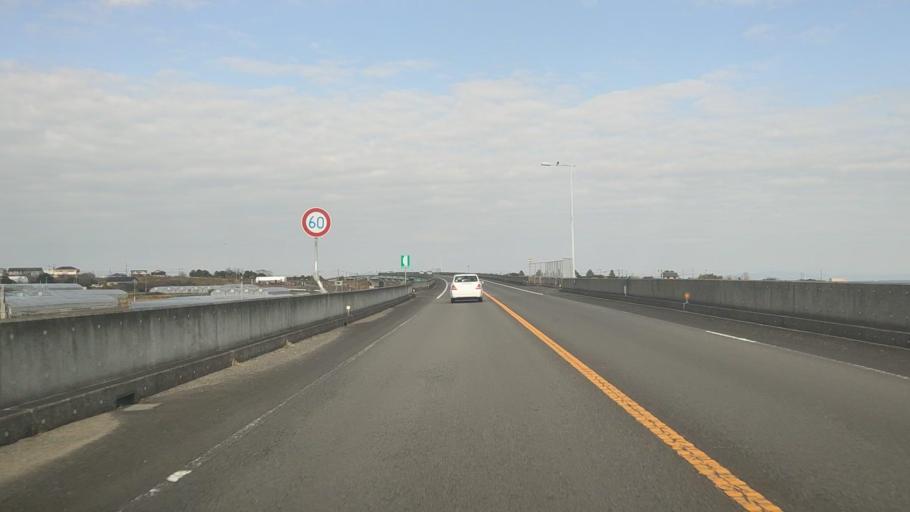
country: JP
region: Nagasaki
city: Shimabara
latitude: 32.7343
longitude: 130.3689
